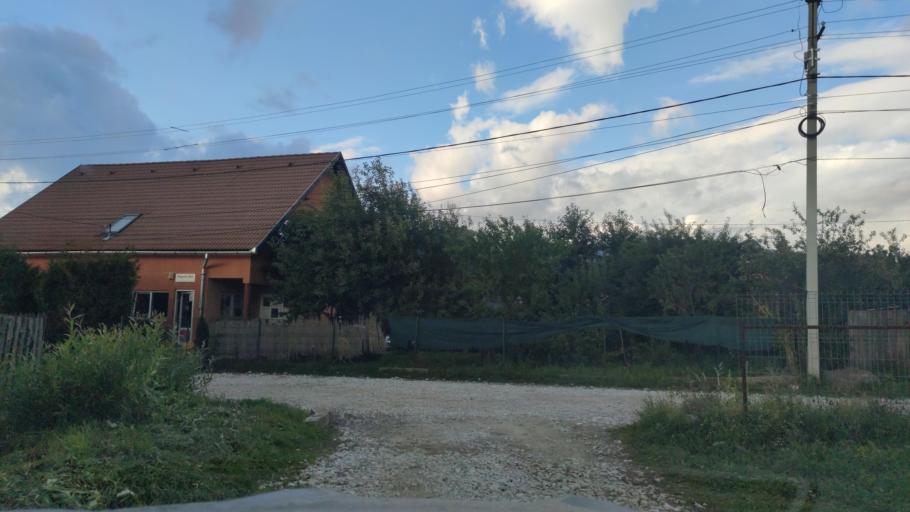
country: RO
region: Harghita
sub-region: Municipiul Gheorgheni
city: Gheorgheni
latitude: 46.7234
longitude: 25.6351
